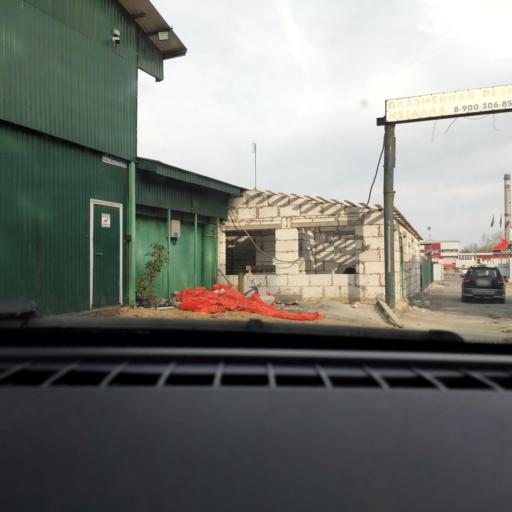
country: RU
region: Voronezj
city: Maslovka
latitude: 51.6026
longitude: 39.2652
